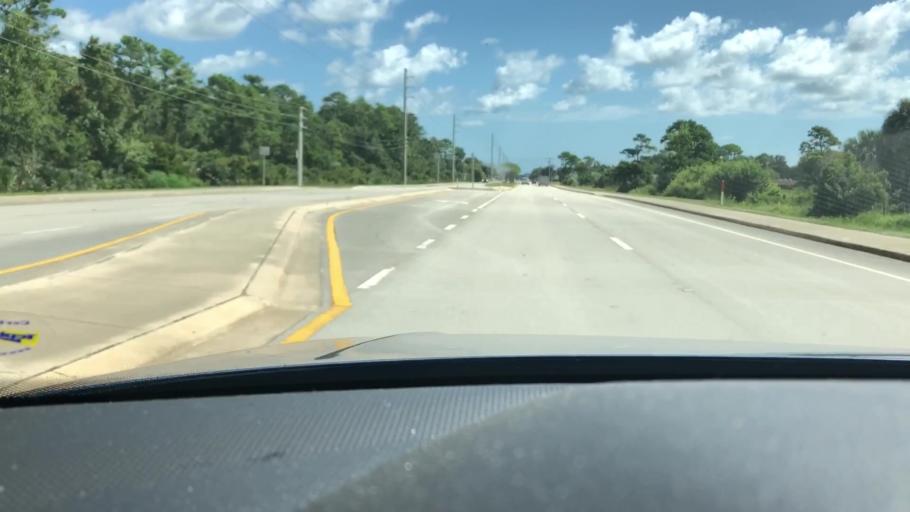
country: US
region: Florida
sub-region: Volusia County
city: Edgewater
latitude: 28.9635
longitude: -80.9202
